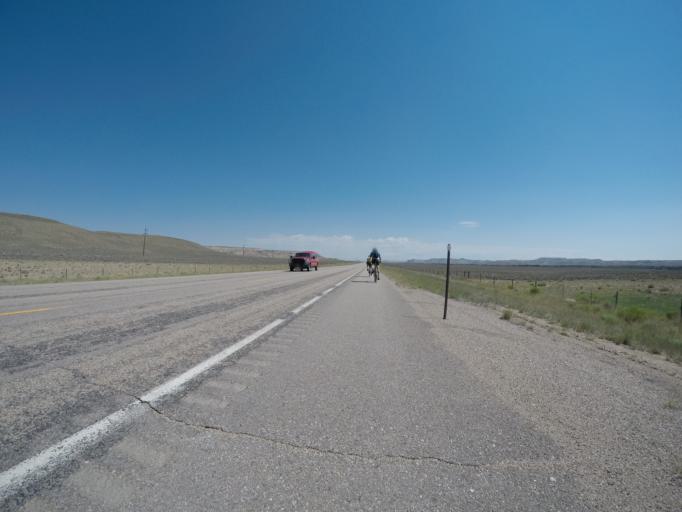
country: US
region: Wyoming
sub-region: Sublette County
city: Marbleton
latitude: 42.3763
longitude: -110.1433
